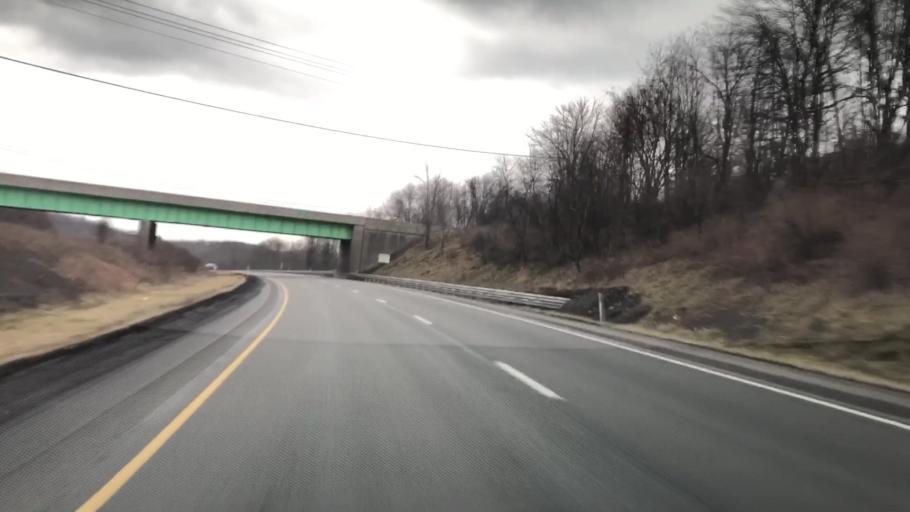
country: US
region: Pennsylvania
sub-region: Butler County
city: Prospect
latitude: 40.9455
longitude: -80.1427
